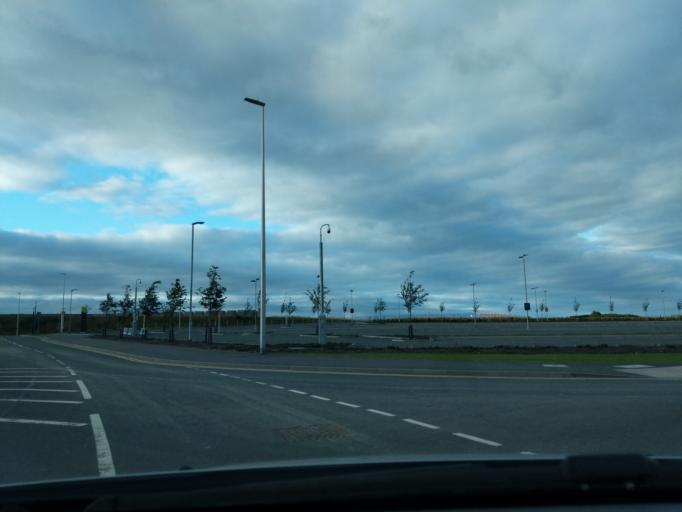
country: GB
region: Scotland
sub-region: Aberdeen City
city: Dyce
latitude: 57.1887
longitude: -2.1927
